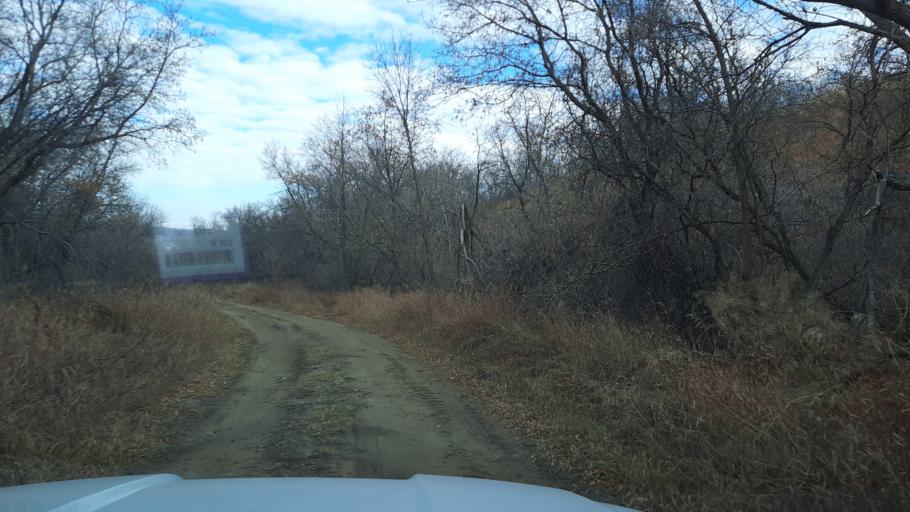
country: CA
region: Saskatchewan
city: Pilot Butte
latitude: 50.7796
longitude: -104.2092
